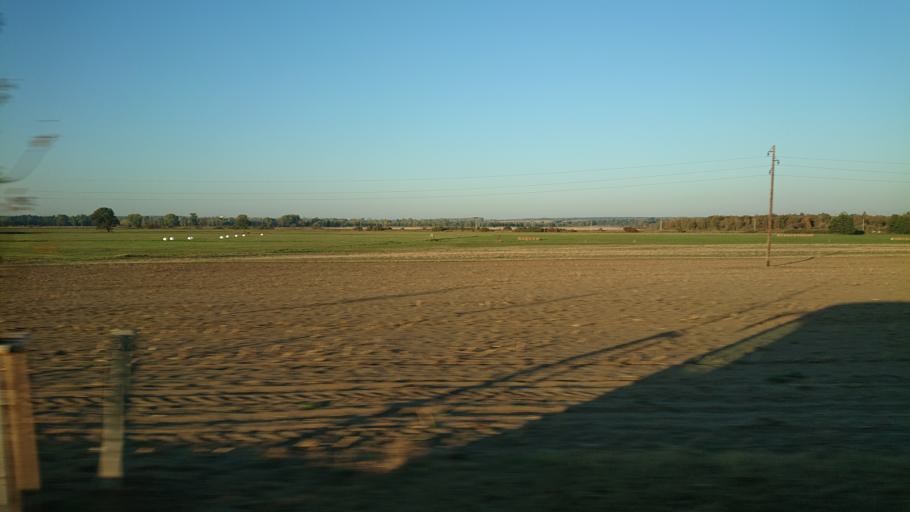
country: DE
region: Mecklenburg-Vorpommern
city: Trollenhagen
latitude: 53.5957
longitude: 13.2720
